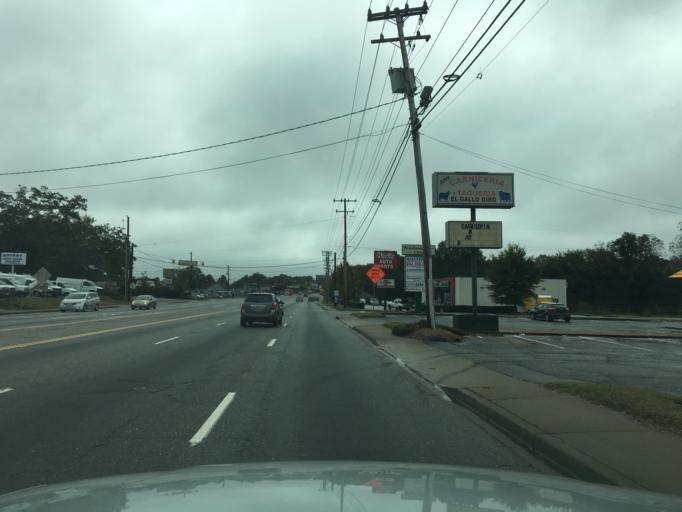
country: US
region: South Carolina
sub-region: Greenville County
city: Welcome
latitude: 34.8191
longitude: -82.4441
